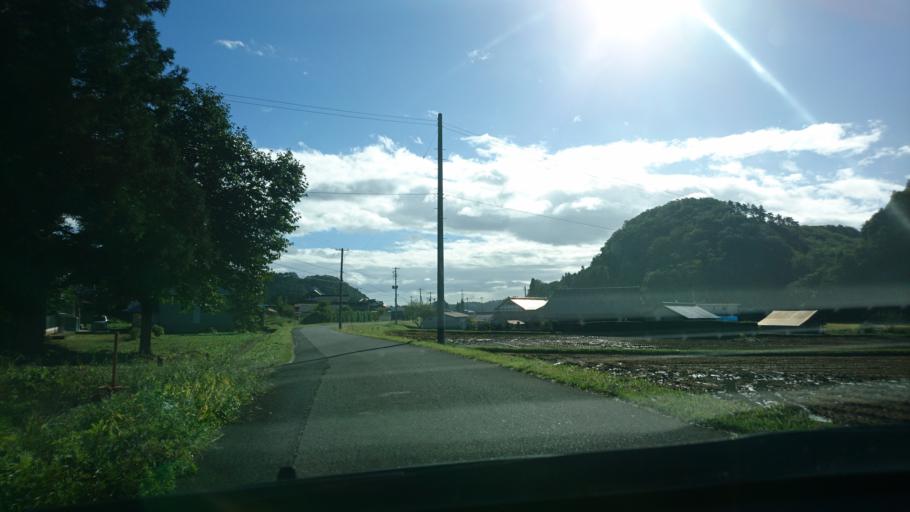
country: JP
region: Iwate
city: Ichinoseki
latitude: 38.9519
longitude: 141.0082
